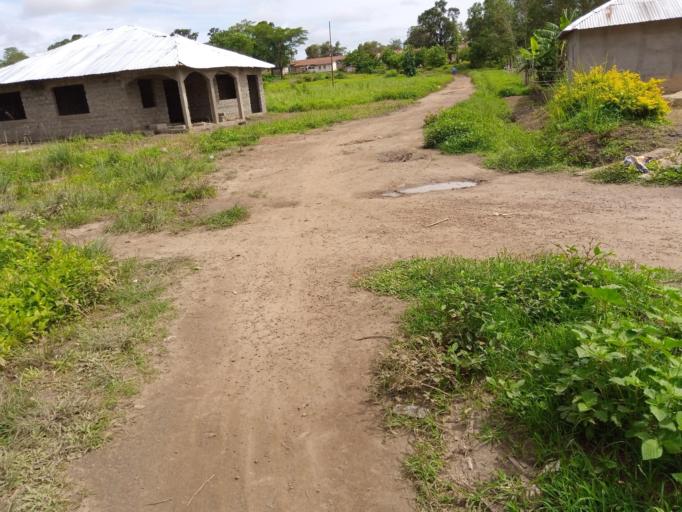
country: SL
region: Southern Province
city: Largo
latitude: 8.1103
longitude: -12.0699
